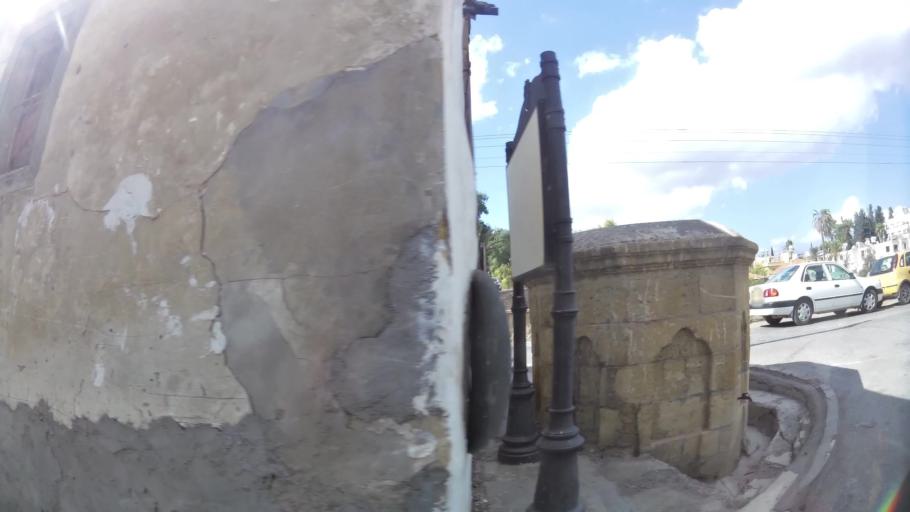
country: CY
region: Lefkosia
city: Nicosia
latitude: 35.1789
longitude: 33.3575
